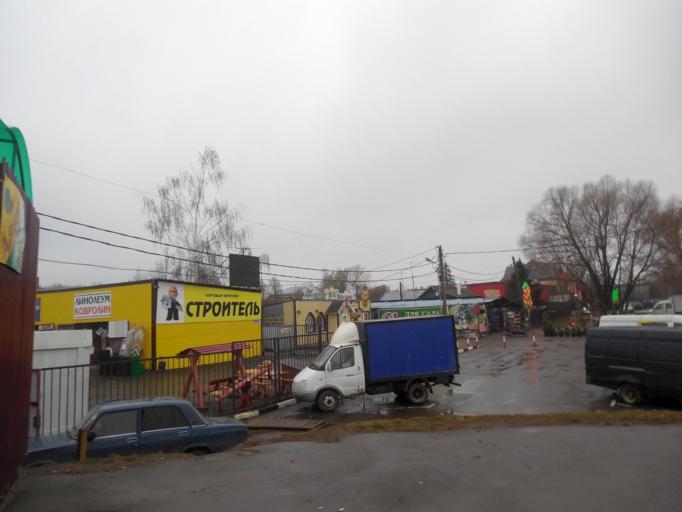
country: RU
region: Moskovskaya
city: Barybino
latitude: 55.2684
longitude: 37.8946
